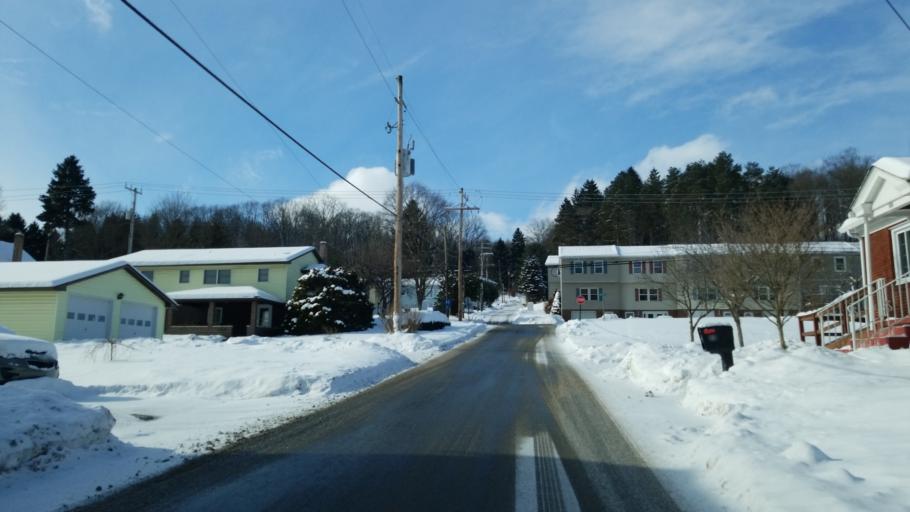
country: US
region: Pennsylvania
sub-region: Clearfield County
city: Clearfield
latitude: 41.0355
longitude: -78.4510
